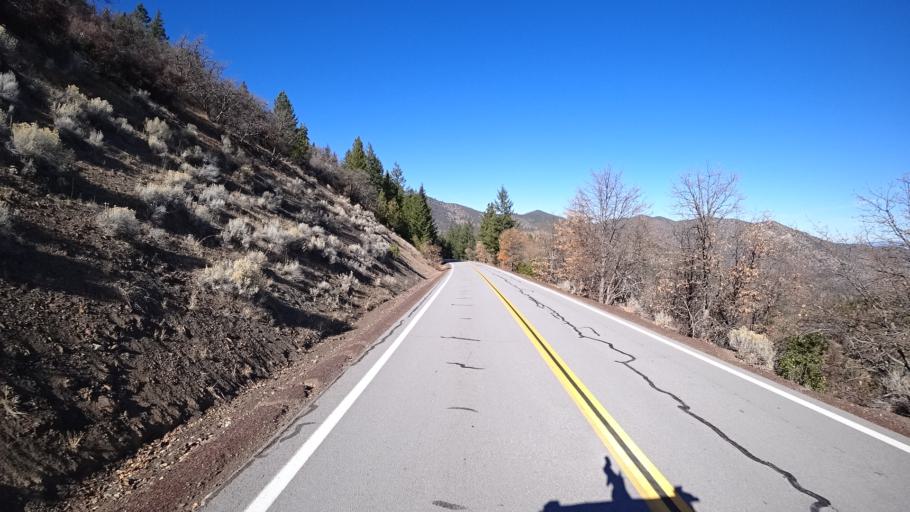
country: US
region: California
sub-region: Siskiyou County
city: Weed
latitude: 41.4416
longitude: -122.6422
